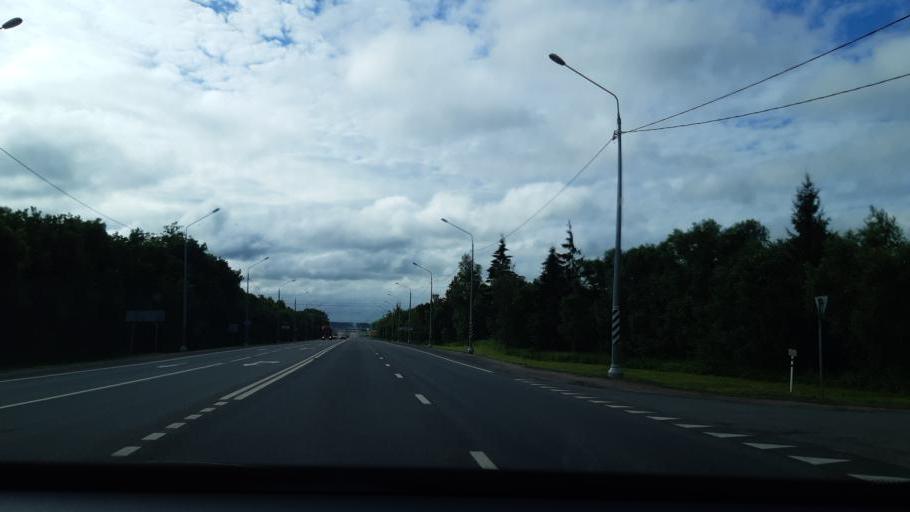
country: RU
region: Smolensk
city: Smolensk
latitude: 54.7158
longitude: 32.1083
